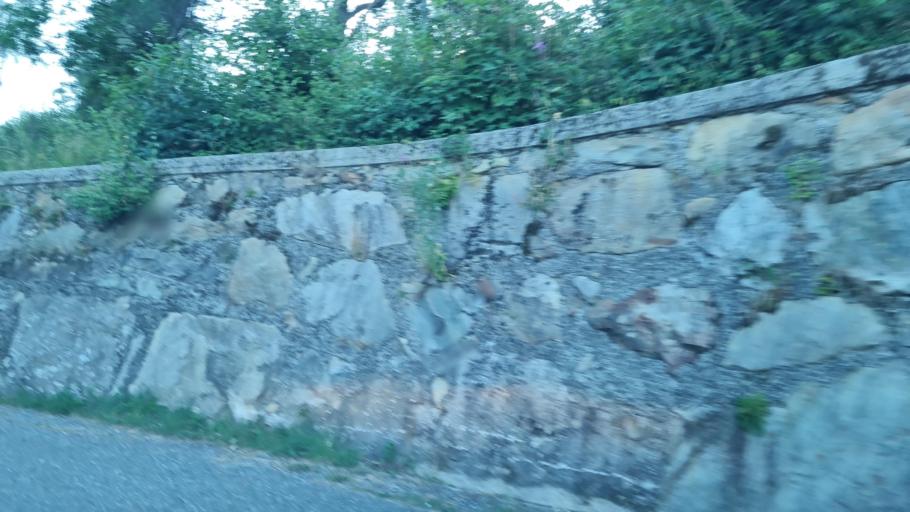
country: IT
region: Aosta Valley
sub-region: Valle d'Aosta
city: Fontainemore
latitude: 45.6306
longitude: 7.8602
